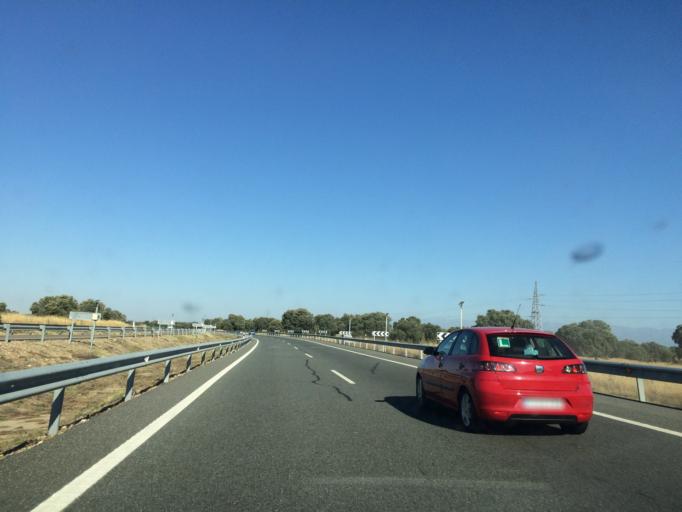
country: ES
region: Castille-La Mancha
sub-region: Province of Toledo
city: Alcanizo
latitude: 39.9225
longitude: -5.0873
